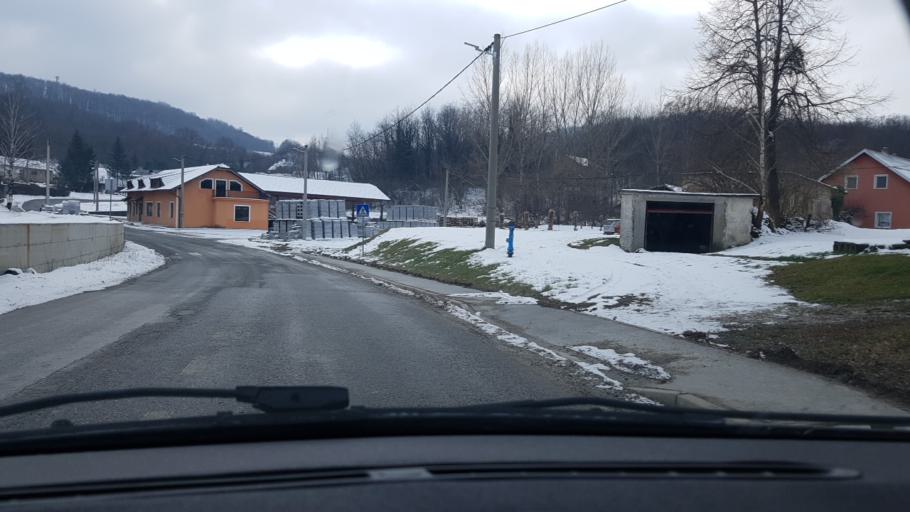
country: HR
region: Krapinsko-Zagorska
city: Mihovljan
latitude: 46.1714
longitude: 15.9805
